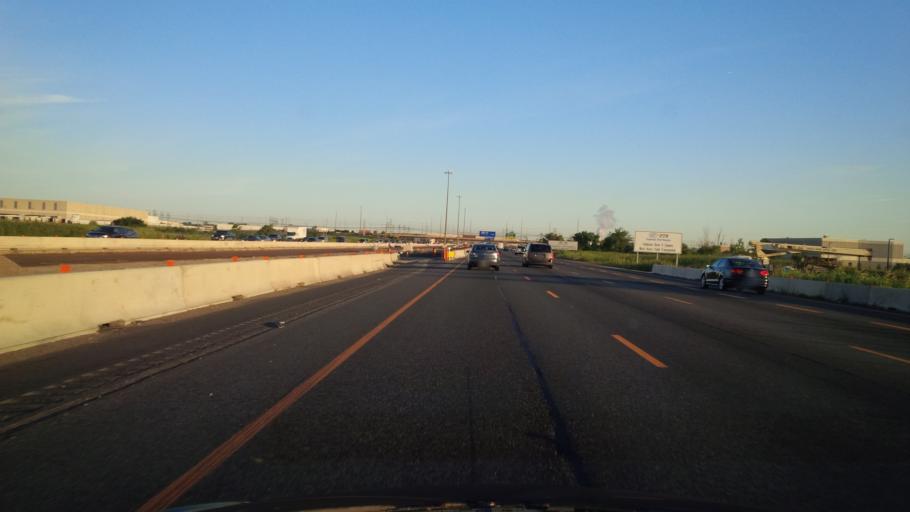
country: CA
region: Ontario
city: Mississauga
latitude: 43.6557
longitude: -79.6822
